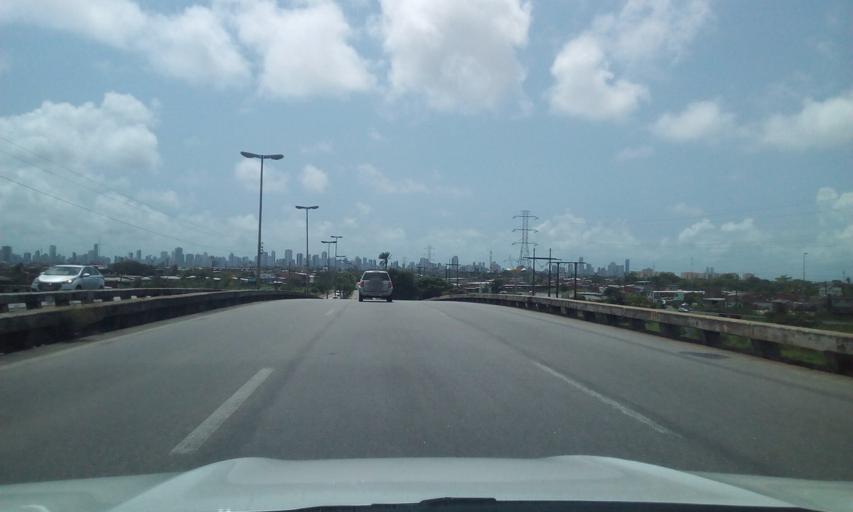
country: BR
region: Pernambuco
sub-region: Recife
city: Recife
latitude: -8.0670
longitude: -34.9426
